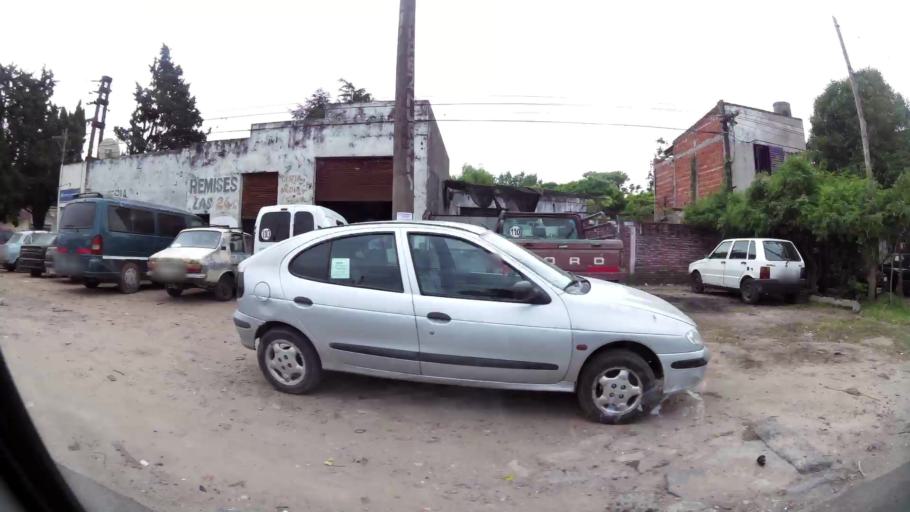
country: AR
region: Buenos Aires
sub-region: Partido de La Plata
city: La Plata
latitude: -34.9258
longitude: -58.0049
